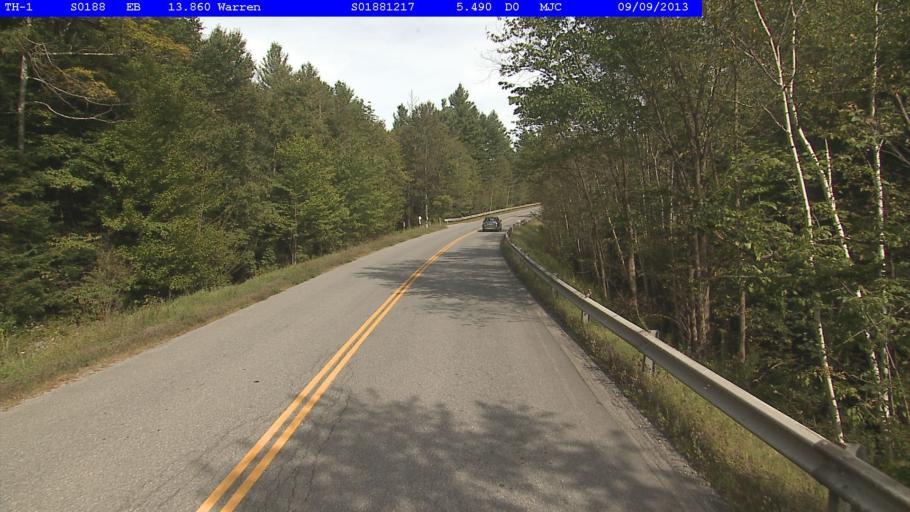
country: US
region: Vermont
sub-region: Washington County
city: Northfield
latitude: 44.1064
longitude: -72.8355
